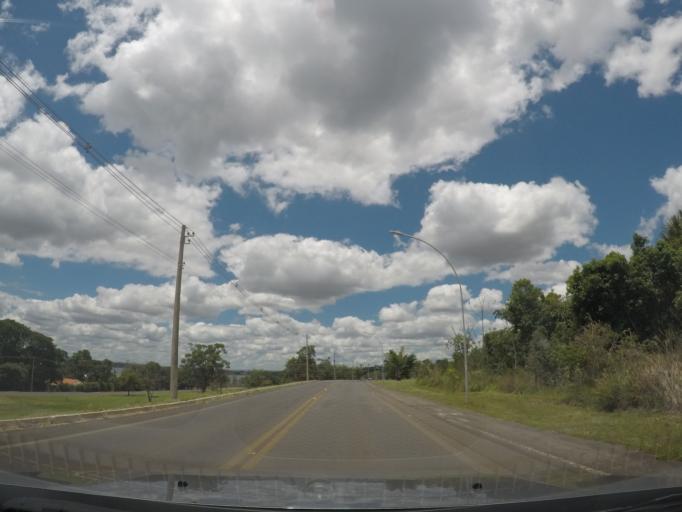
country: BR
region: Federal District
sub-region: Brasilia
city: Brasilia
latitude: -15.7818
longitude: -47.8073
